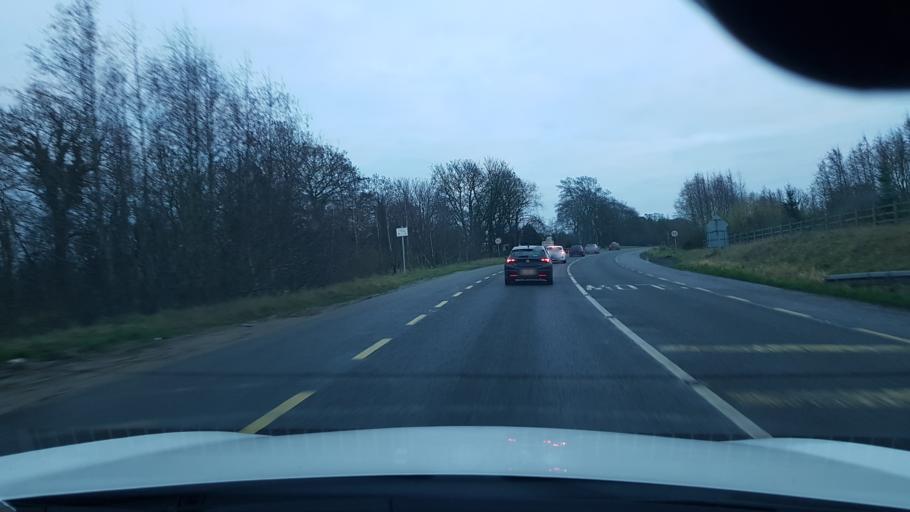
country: IE
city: Kentstown
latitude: 53.5981
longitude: -6.6108
